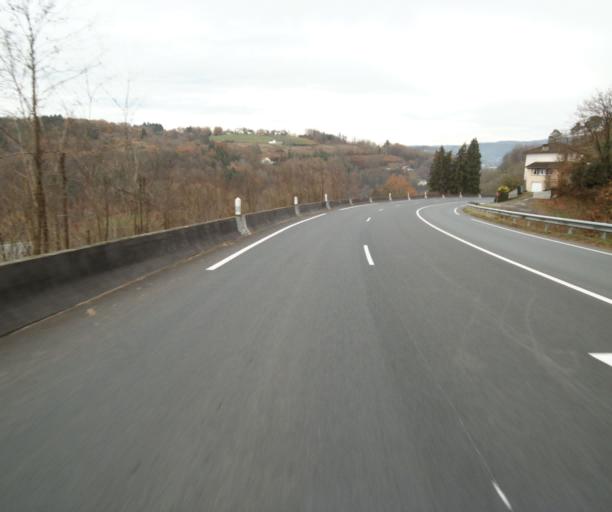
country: FR
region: Limousin
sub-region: Departement de la Correze
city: Tulle
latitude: 45.2694
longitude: 1.7390
